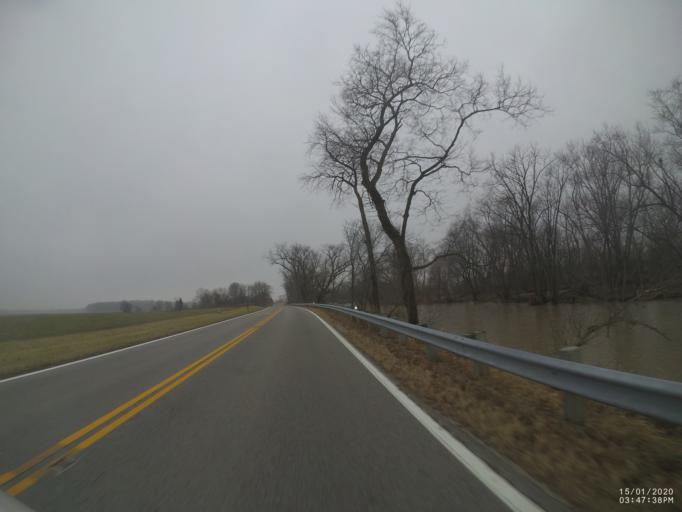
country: US
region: Ohio
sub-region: Sandusky County
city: Woodville
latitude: 41.4393
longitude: -83.3891
